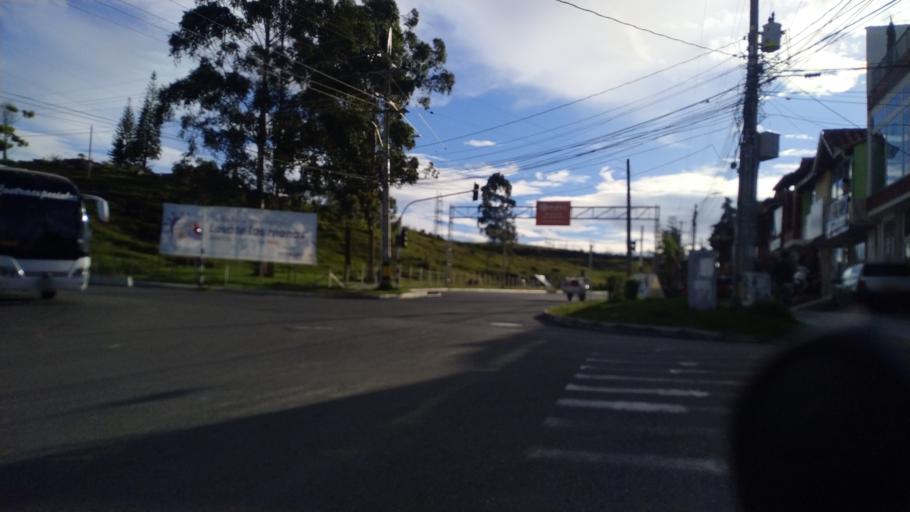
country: CO
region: Antioquia
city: Rionegro
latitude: 6.1491
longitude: -75.3788
